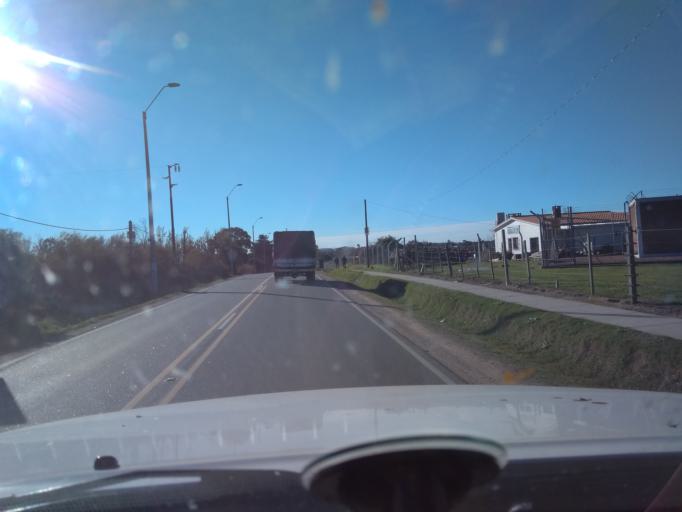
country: UY
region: Canelones
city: Joaquin Suarez
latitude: -34.7601
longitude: -56.0181
